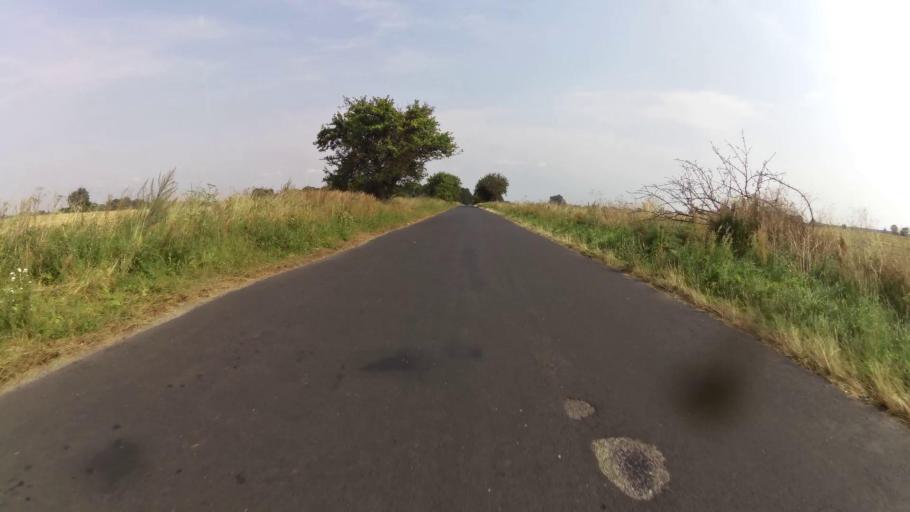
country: PL
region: West Pomeranian Voivodeship
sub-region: Powiat pyrzycki
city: Lipiany
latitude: 52.9713
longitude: 14.9808
